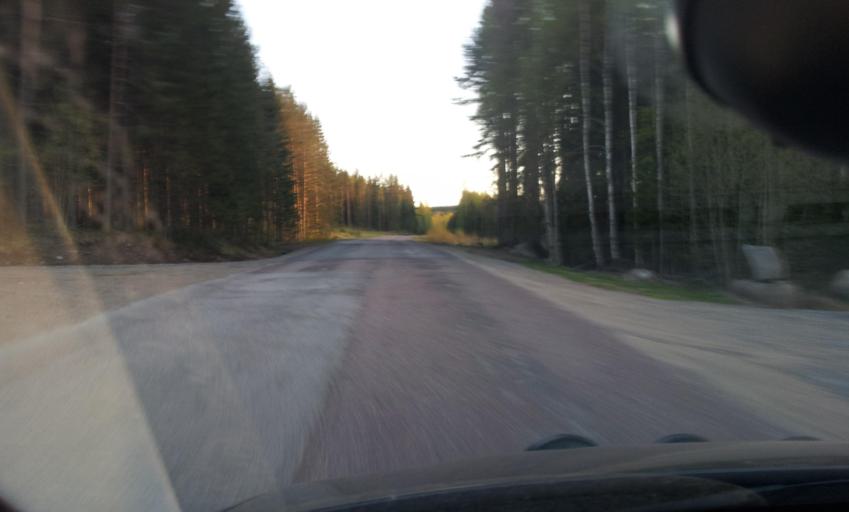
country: SE
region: Gaevleborg
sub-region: Bollnas Kommun
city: Bollnas
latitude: 61.3932
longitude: 16.4914
